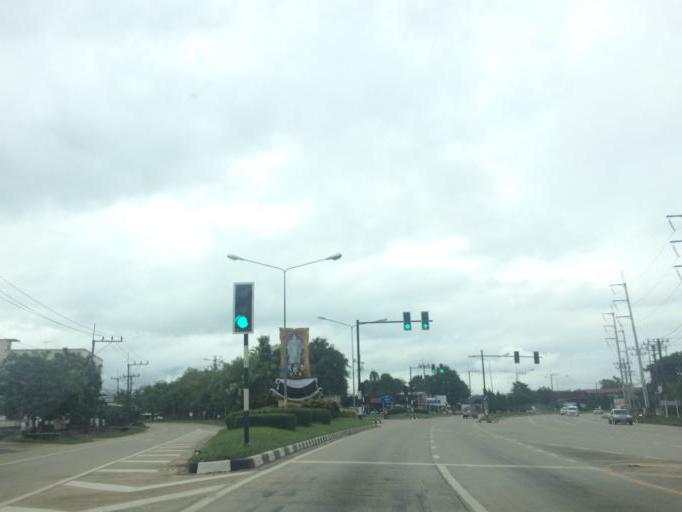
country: TH
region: Chiang Rai
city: Mae Chan
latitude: 20.1374
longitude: 99.8574
